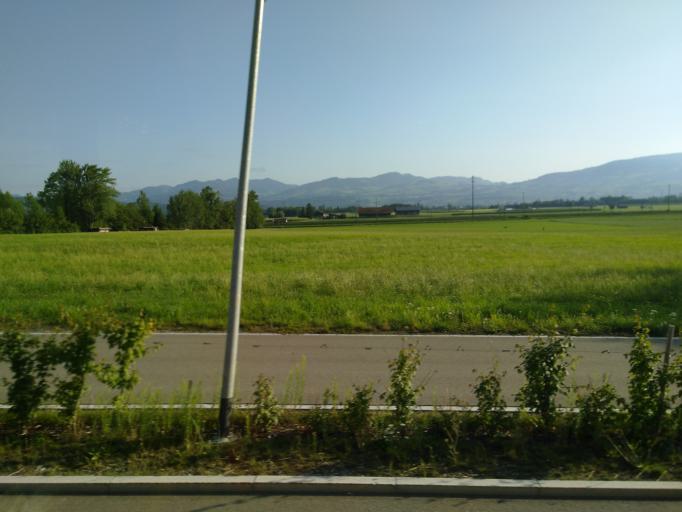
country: CH
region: Schwyz
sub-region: Bezirk March
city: Reichenburg
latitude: 47.1726
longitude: 8.9624
